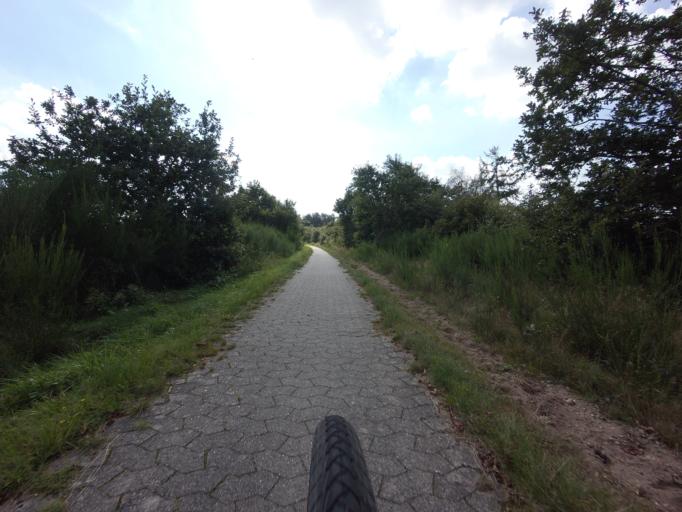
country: DK
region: Central Jutland
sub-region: Viborg Kommune
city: Viborg
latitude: 56.3788
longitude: 9.2902
